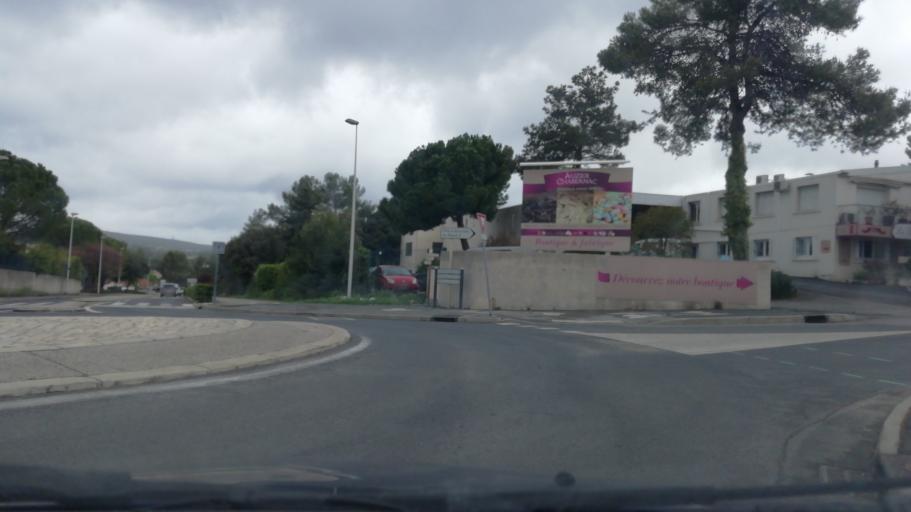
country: FR
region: Languedoc-Roussillon
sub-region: Departement de l'Herault
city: Saint-Gely-du-Fesc
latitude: 43.6818
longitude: 3.8106
